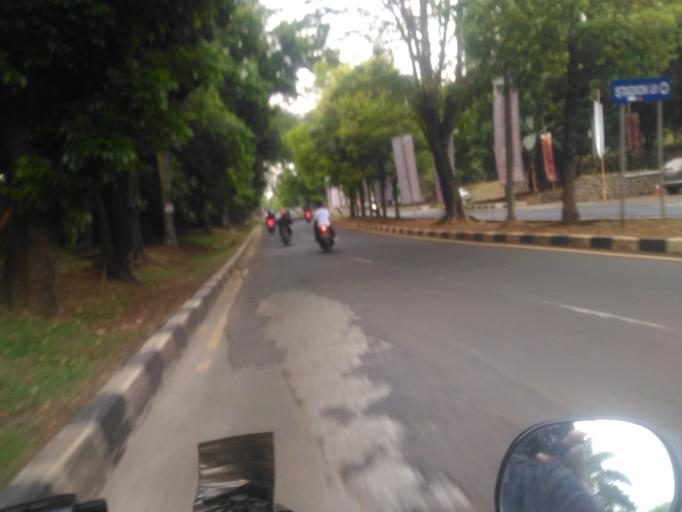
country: ID
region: West Java
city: Depok
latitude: -6.3654
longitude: 106.8215
